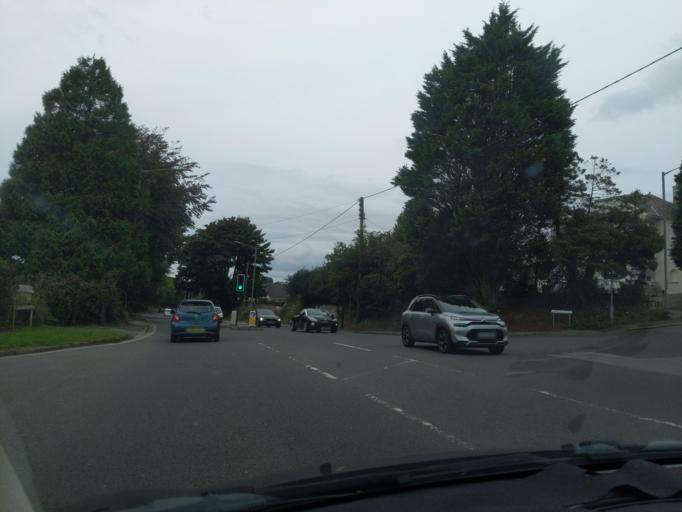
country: GB
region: England
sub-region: Cornwall
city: St Austell
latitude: 50.3339
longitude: -4.7863
